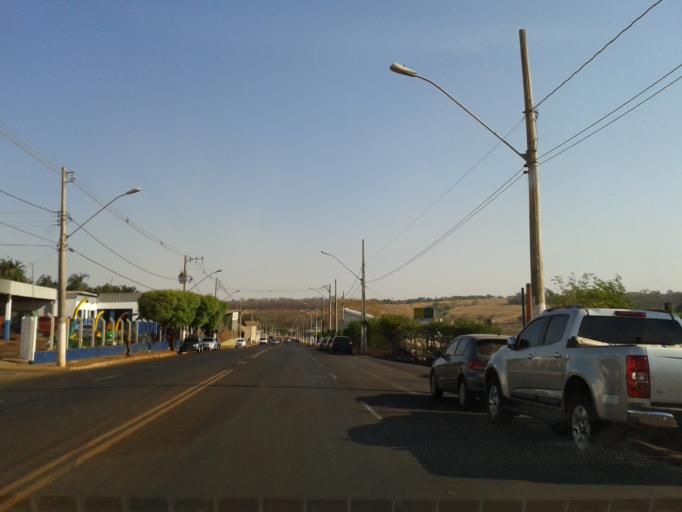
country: BR
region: Minas Gerais
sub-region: Ituiutaba
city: Ituiutaba
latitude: -18.9530
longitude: -49.4570
